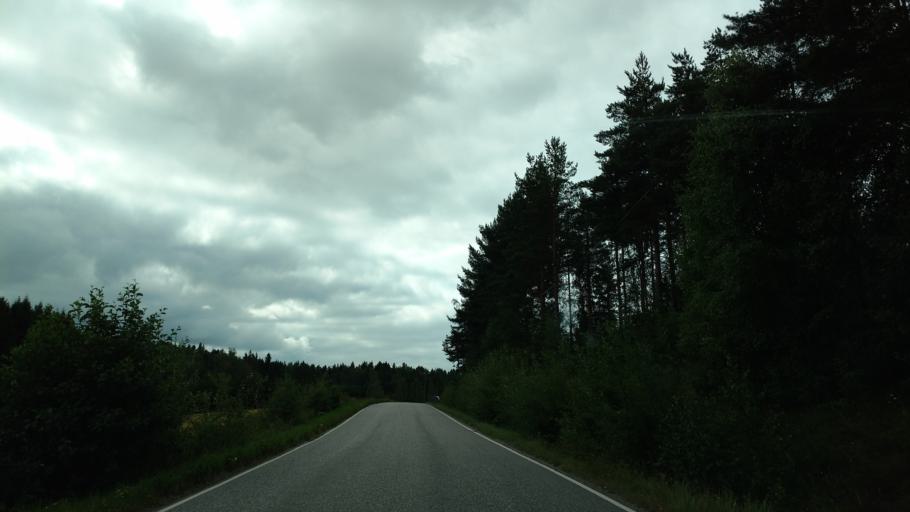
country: FI
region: Varsinais-Suomi
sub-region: Aboland-Turunmaa
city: Dragsfjaerd
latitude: 60.0473
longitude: 22.4522
